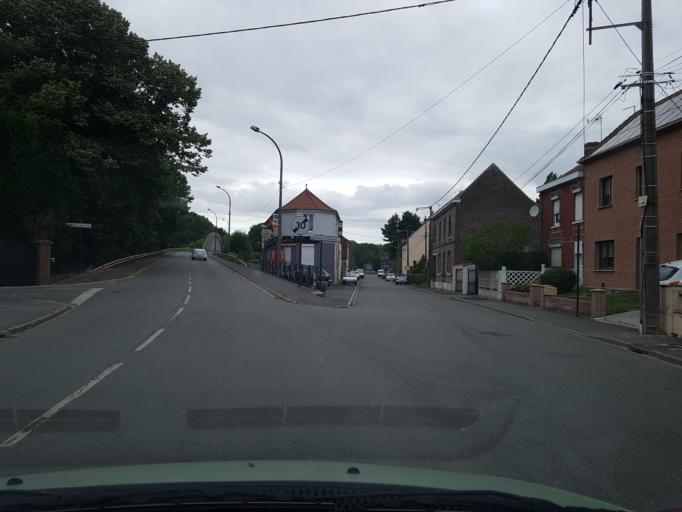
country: FR
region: Nord-Pas-de-Calais
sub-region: Departement du Pas-de-Calais
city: Meurchin
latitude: 50.4973
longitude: 2.8828
